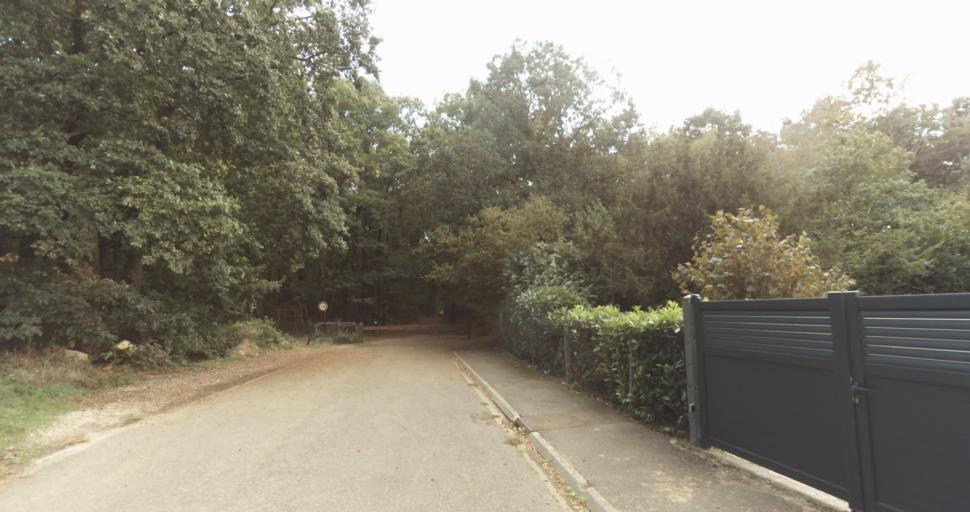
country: FR
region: Centre
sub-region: Departement d'Eure-et-Loir
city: Garnay
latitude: 48.7242
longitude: 1.3344
